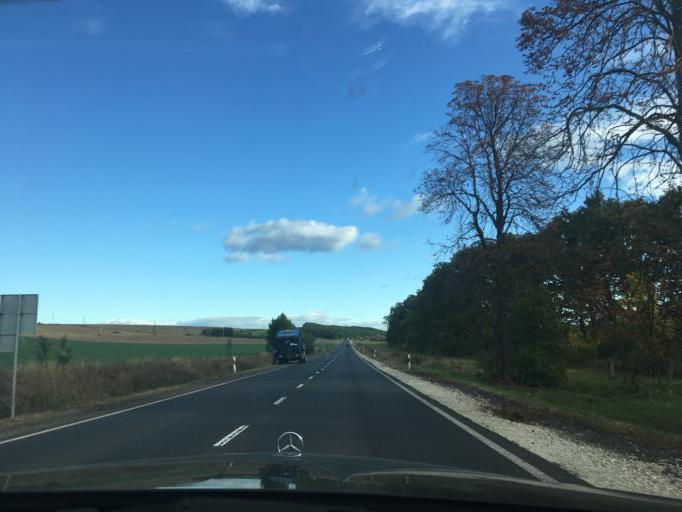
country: HU
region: Borsod-Abauj-Zemplen
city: Encs
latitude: 48.3659
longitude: 21.1404
